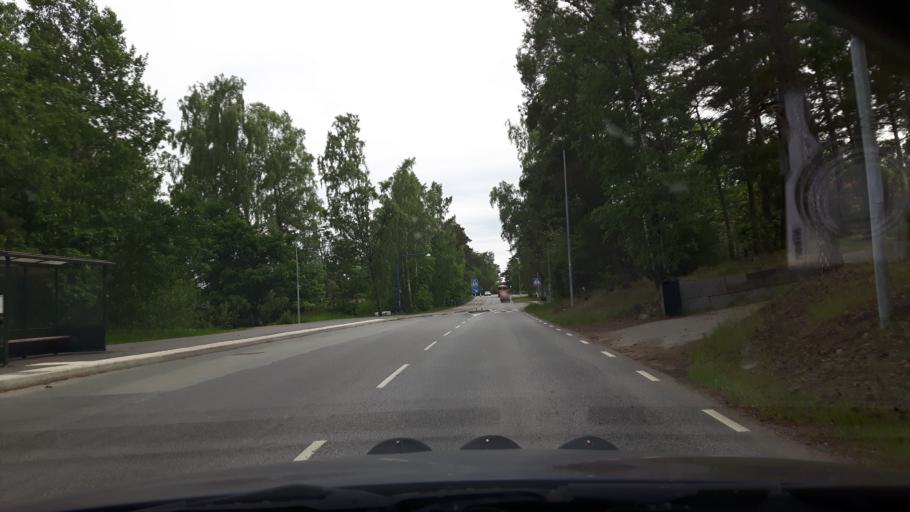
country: SE
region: Stockholm
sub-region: Haninge Kommun
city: Haninge
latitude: 59.1862
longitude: 18.1841
